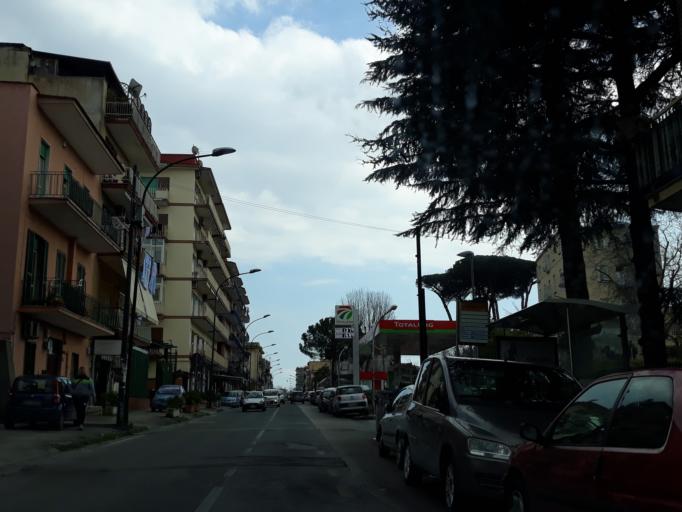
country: IT
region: Campania
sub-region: Provincia di Napoli
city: Napoli
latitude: 40.8829
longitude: 14.2311
